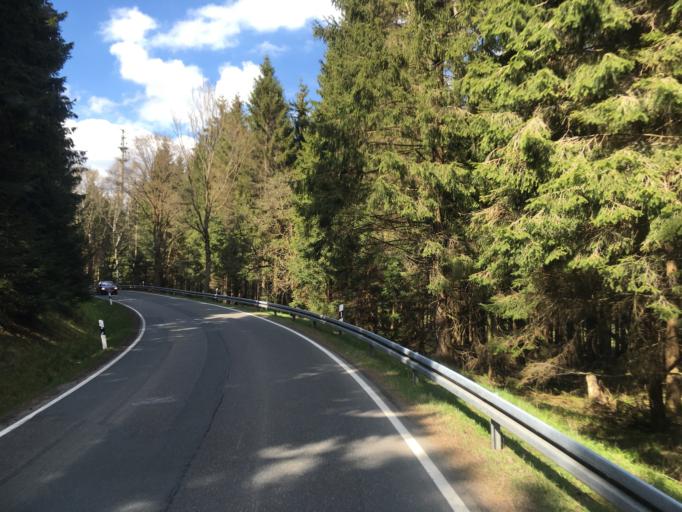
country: DE
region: Lower Saxony
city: Braunlage
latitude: 51.7551
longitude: 10.6851
